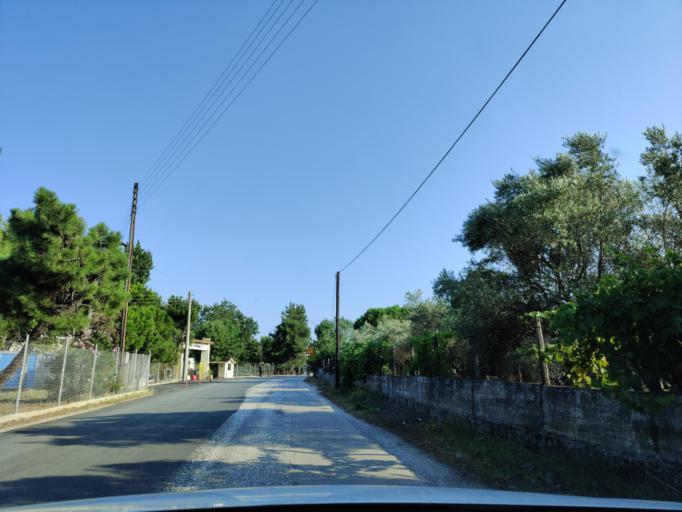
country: GR
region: East Macedonia and Thrace
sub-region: Nomos Kavalas
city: Nea Peramos
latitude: 40.8289
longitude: 24.3051
